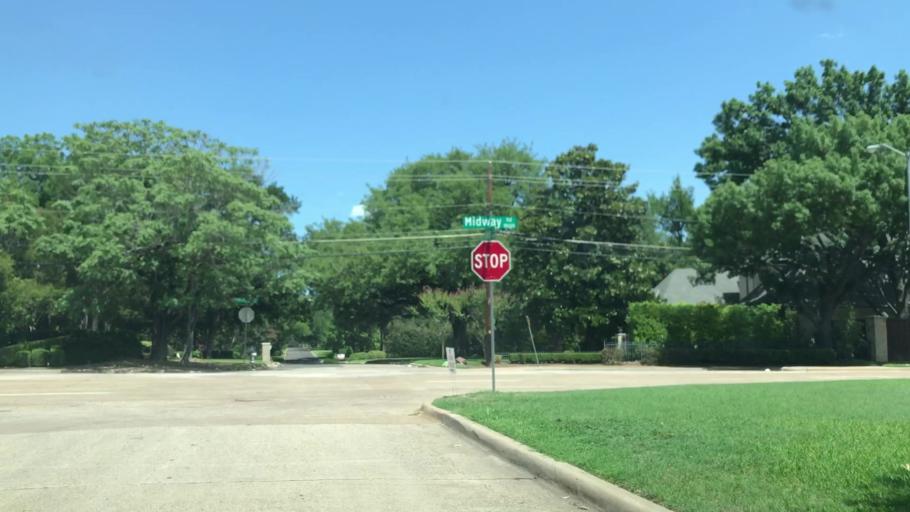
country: US
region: Texas
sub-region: Dallas County
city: University Park
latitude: 32.8727
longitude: -96.8389
